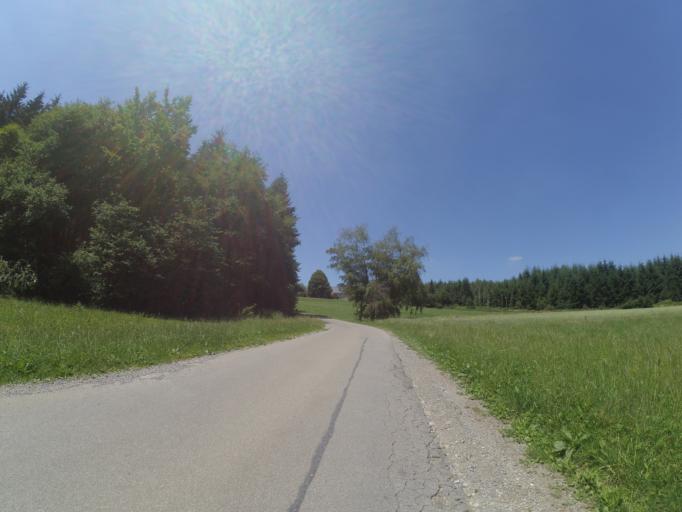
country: DE
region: Baden-Wuerttemberg
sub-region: Tuebingen Region
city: Bad Waldsee
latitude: 47.9033
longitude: 9.8195
